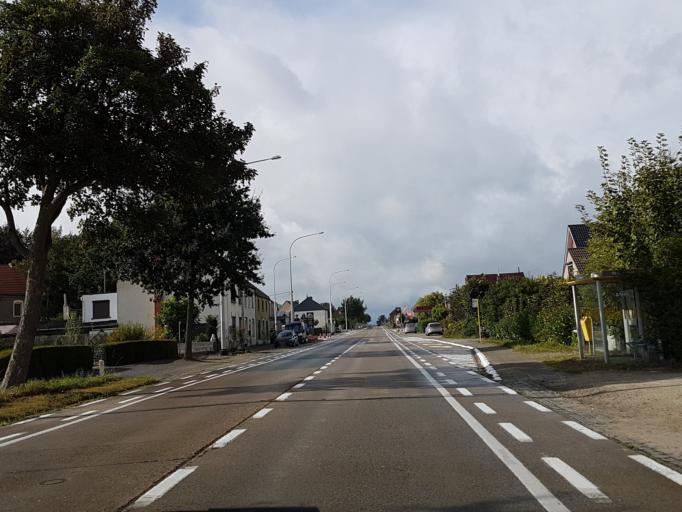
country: BE
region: Flanders
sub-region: Provincie Vlaams-Brabant
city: Boutersem
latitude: 50.8437
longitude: 4.8288
